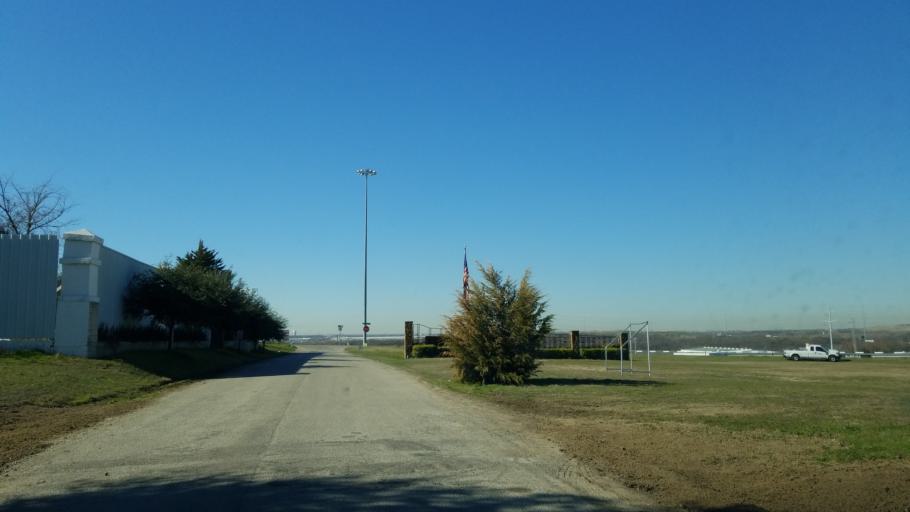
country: US
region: Texas
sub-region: Dallas County
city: Cockrell Hill
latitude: 32.7589
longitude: -96.9155
